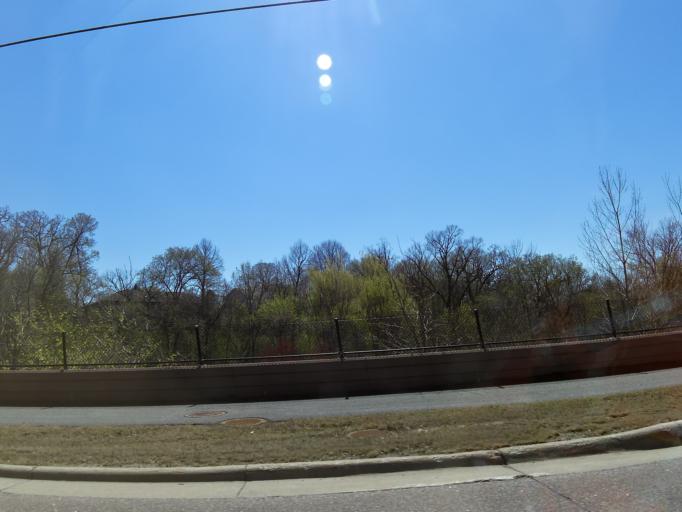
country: US
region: Minnesota
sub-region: Hennepin County
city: Eden Prairie
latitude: 44.8273
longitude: -93.4225
